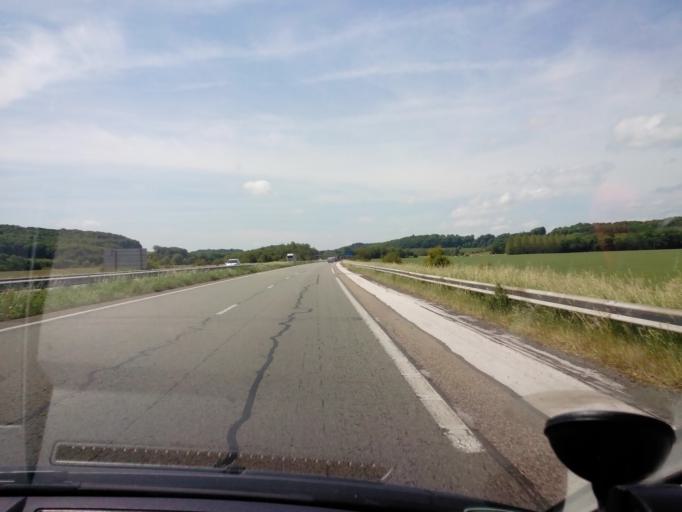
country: FR
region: Champagne-Ardenne
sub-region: Departement de la Haute-Marne
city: Avrecourt
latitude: 47.9847
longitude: 5.5064
